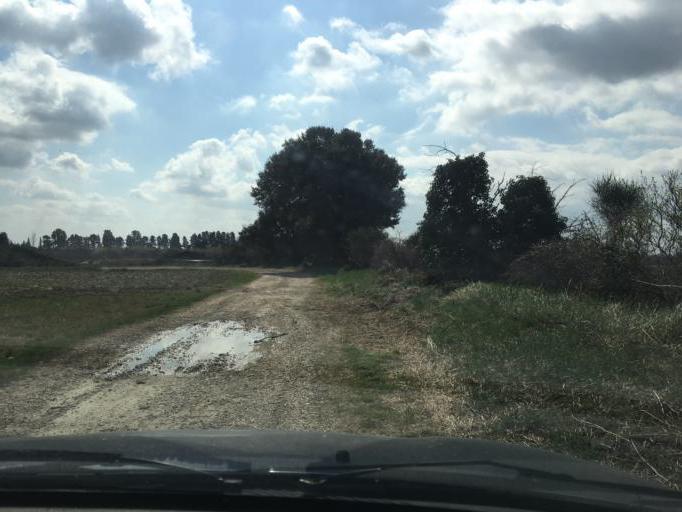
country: FR
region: Provence-Alpes-Cote d'Azur
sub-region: Departement du Vaucluse
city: Orange
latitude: 44.1665
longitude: 4.8209
